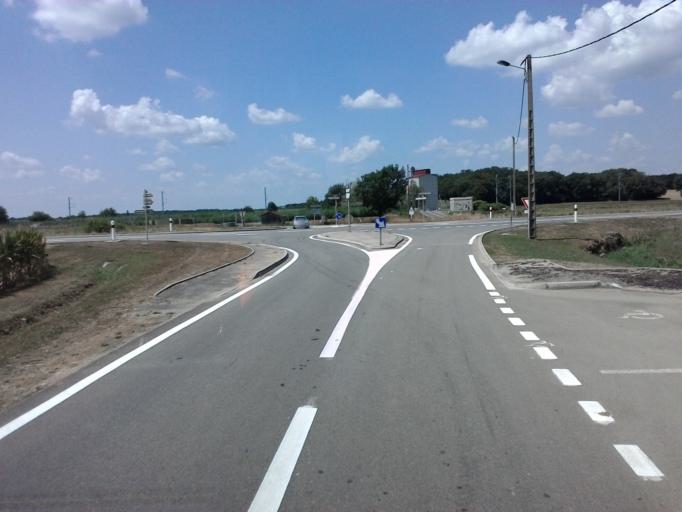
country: FR
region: Franche-Comte
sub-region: Departement du Jura
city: Cousance
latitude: 46.5823
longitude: 5.4438
